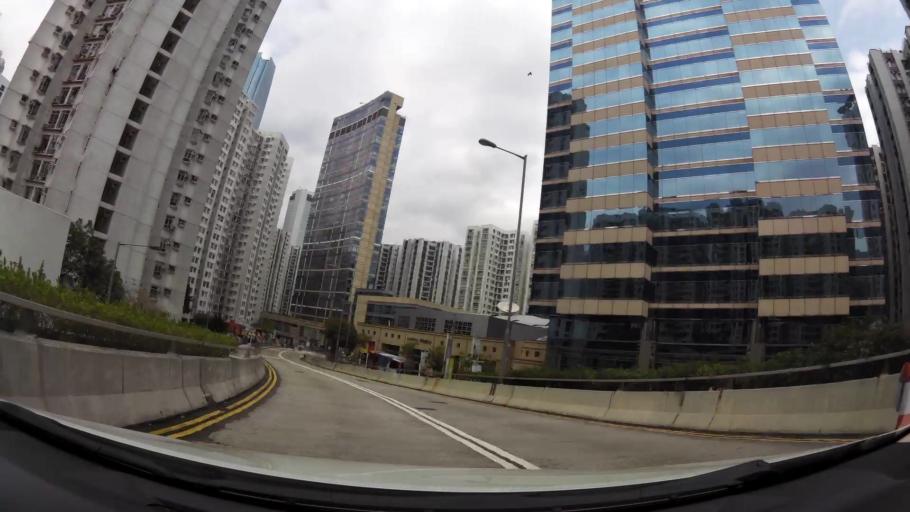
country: HK
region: Wanchai
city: Wan Chai
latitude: 22.2850
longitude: 114.2180
